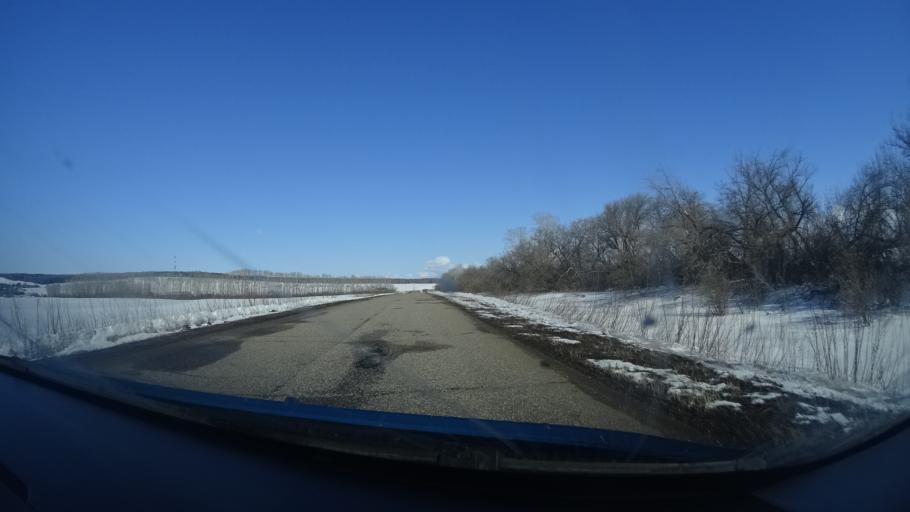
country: RU
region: Bashkortostan
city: Chishmy
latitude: 54.5977
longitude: 55.3428
